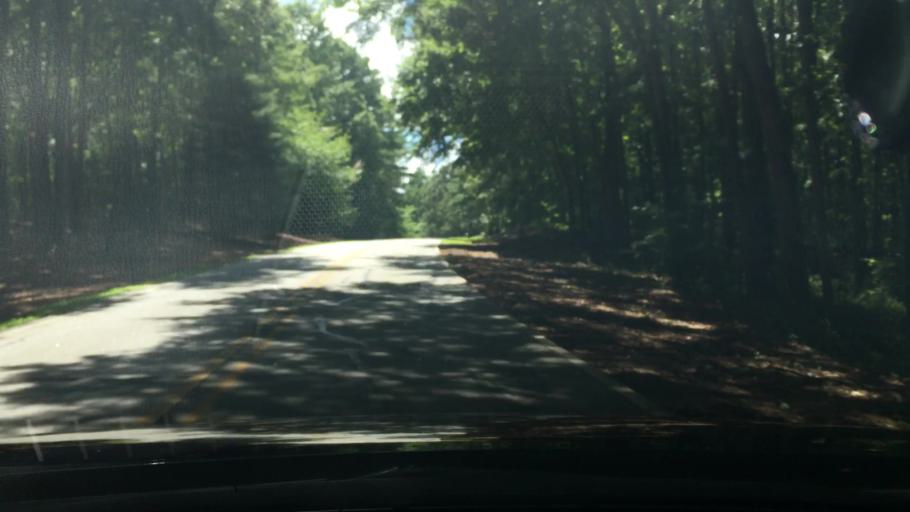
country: US
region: Georgia
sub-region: Putnam County
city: Jefferson
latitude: 33.3931
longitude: -83.2374
